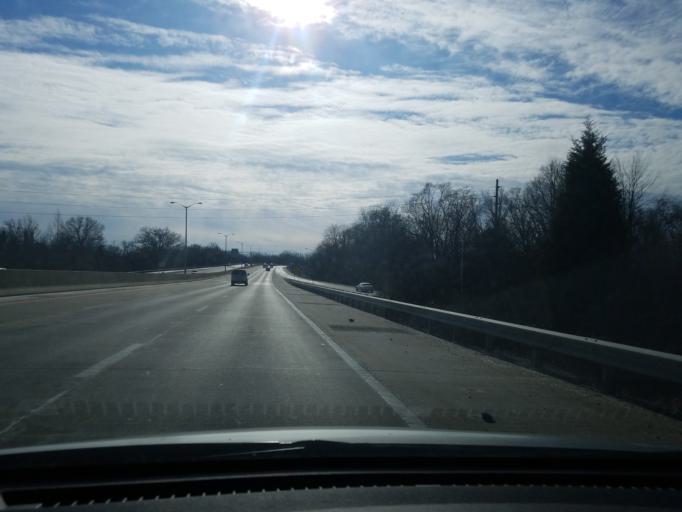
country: US
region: Indiana
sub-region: Floyd County
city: New Albany
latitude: 38.2536
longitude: -85.8062
